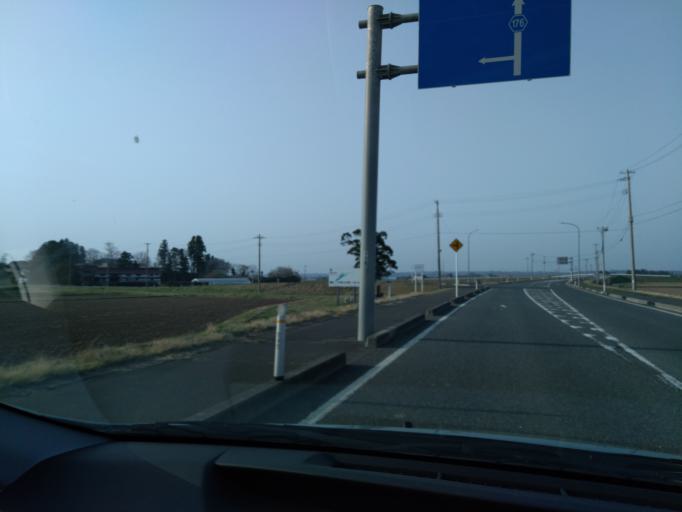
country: JP
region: Iwate
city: Ichinoseki
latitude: 38.7452
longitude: 141.1314
